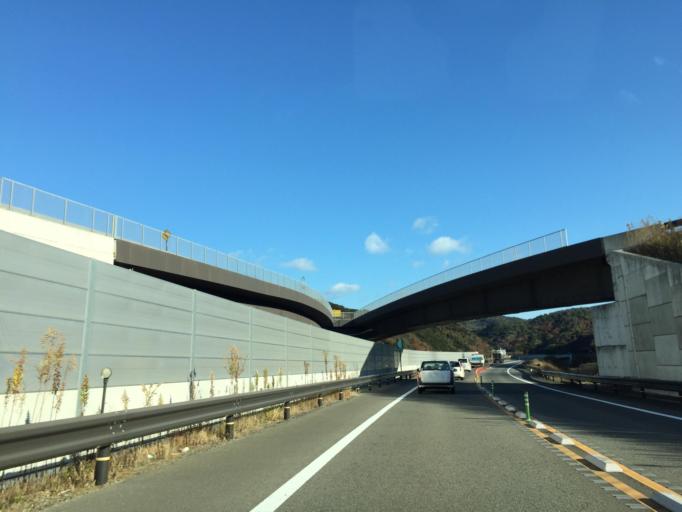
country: JP
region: Wakayama
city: Wakayama-shi
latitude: 34.2988
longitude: 135.1543
